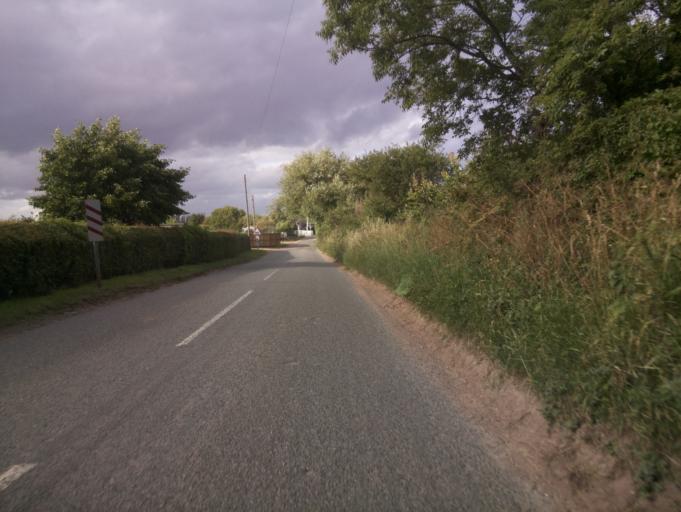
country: GB
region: England
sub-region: Gloucestershire
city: Chipping Campden
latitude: 52.0299
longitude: -1.7342
